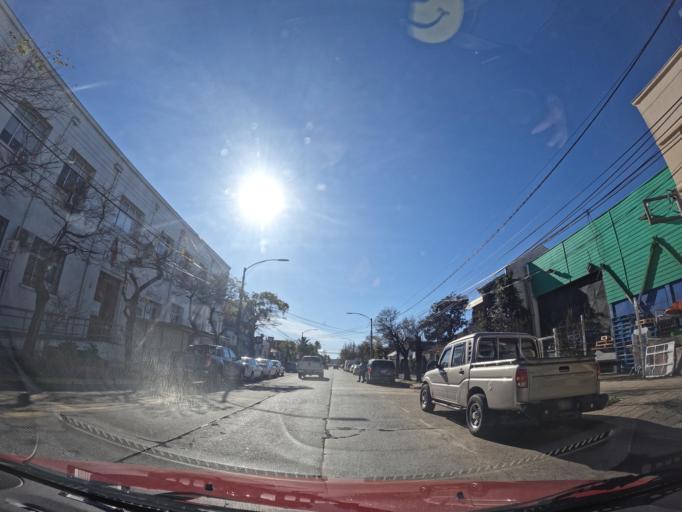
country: CL
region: Maule
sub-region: Provincia de Cauquenes
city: Cauquenes
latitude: -35.9662
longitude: -72.3147
